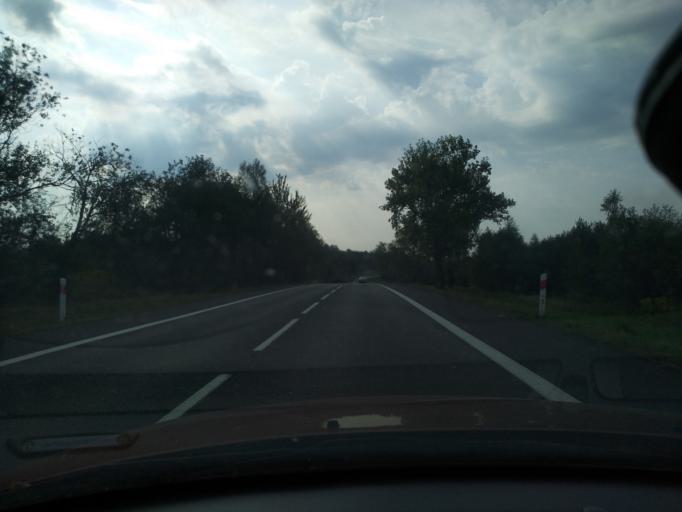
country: PL
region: Lower Silesian Voivodeship
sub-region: Powiat lubanski
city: Luban
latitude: 51.0940
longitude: 15.3179
